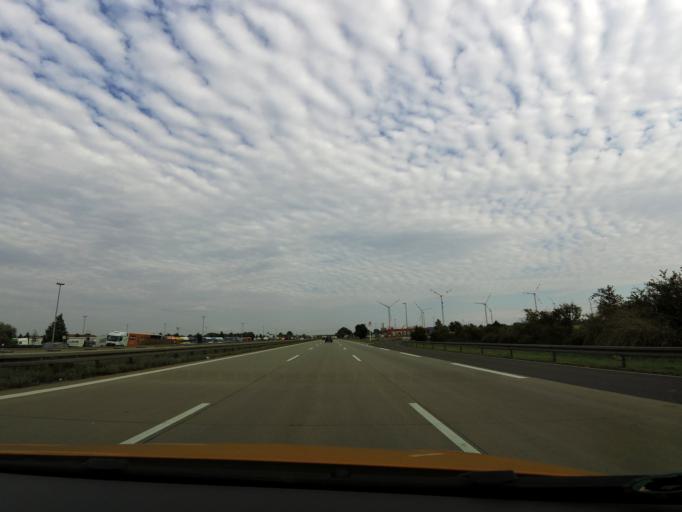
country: DE
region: Saxony-Anhalt
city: Gross Santersleben
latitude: 52.1856
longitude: 11.4473
